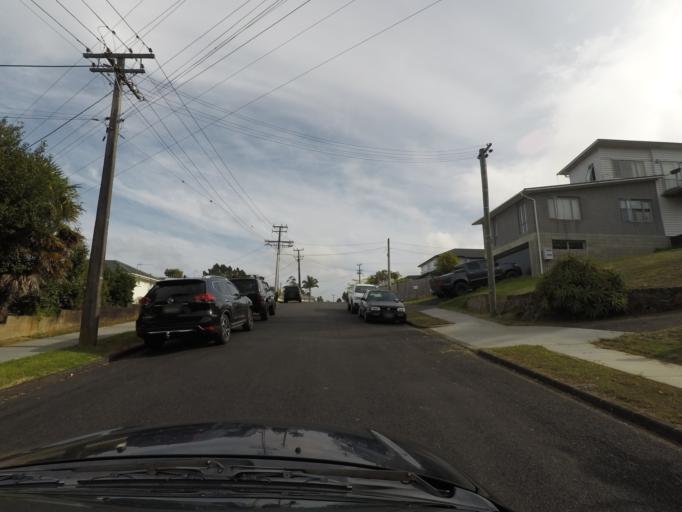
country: NZ
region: Auckland
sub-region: Auckland
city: Rosebank
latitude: -36.8978
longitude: 174.6708
